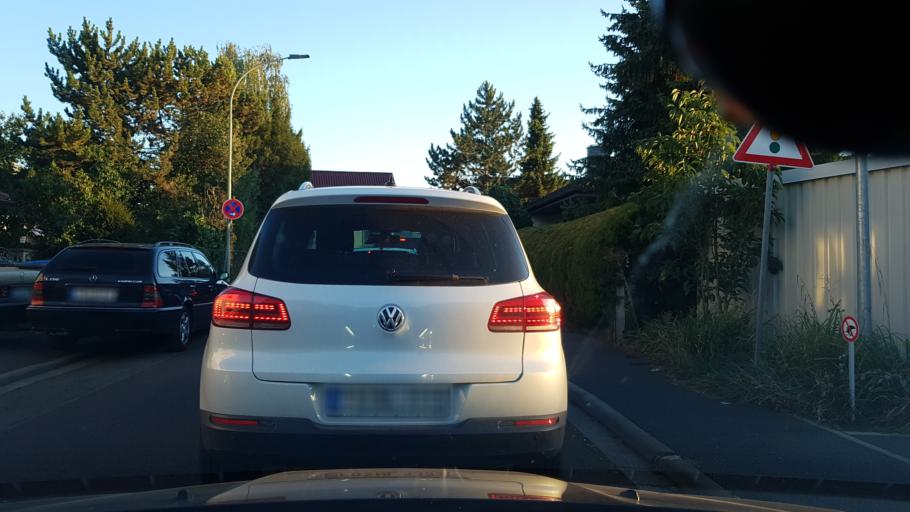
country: DE
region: Hesse
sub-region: Regierungsbezirk Darmstadt
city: Karben
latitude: 50.2212
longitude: 8.7788
